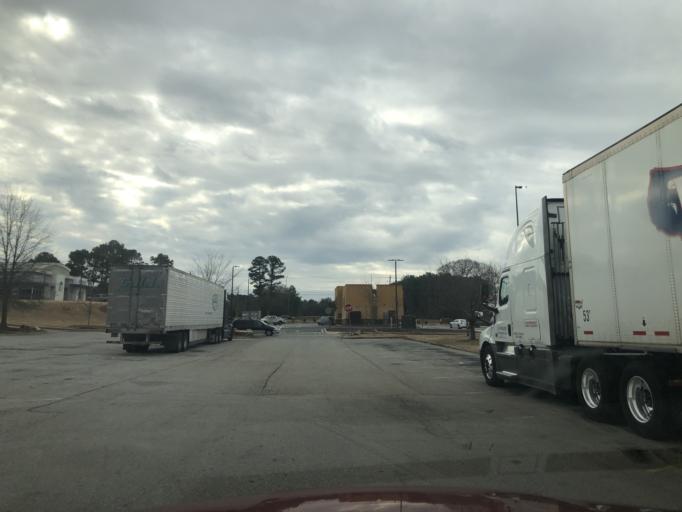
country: US
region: Georgia
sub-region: Clayton County
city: Conley
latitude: 33.6353
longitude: -84.2916
